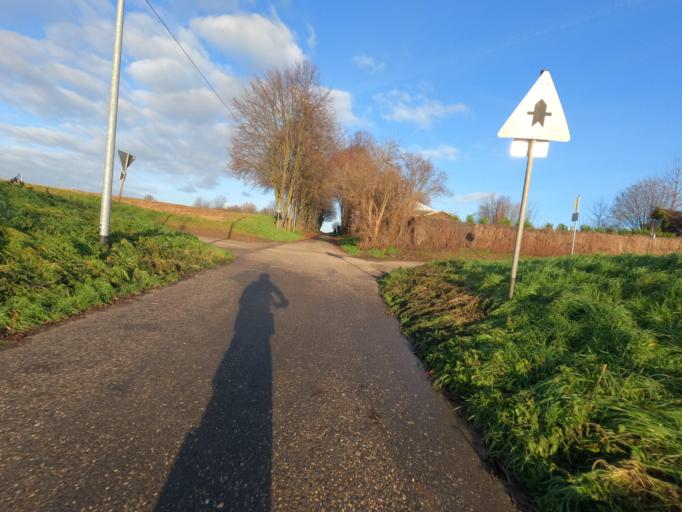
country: DE
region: North Rhine-Westphalia
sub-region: Regierungsbezirk Koln
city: Bedburg
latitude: 50.9688
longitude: 6.5420
